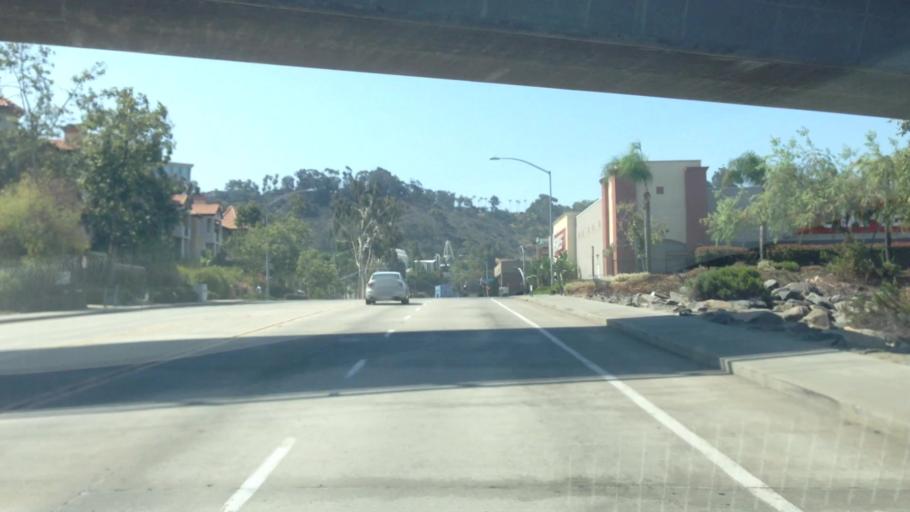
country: US
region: California
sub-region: San Diego County
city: San Diego
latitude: 32.7724
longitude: -117.1448
